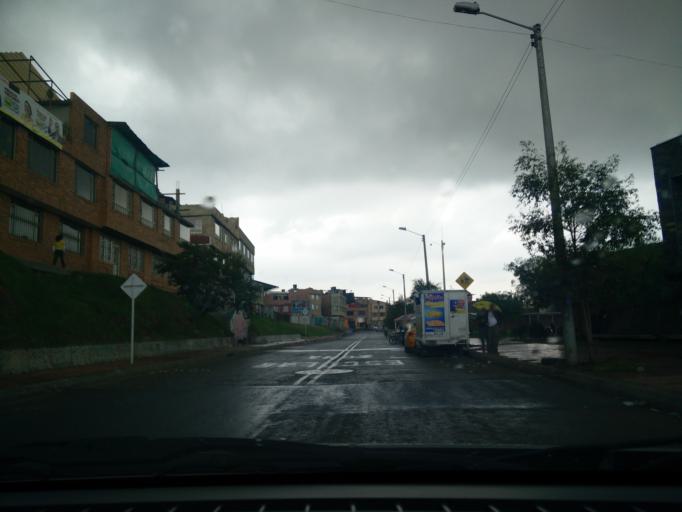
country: CO
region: Cundinamarca
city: Cota
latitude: 4.7491
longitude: -74.1147
